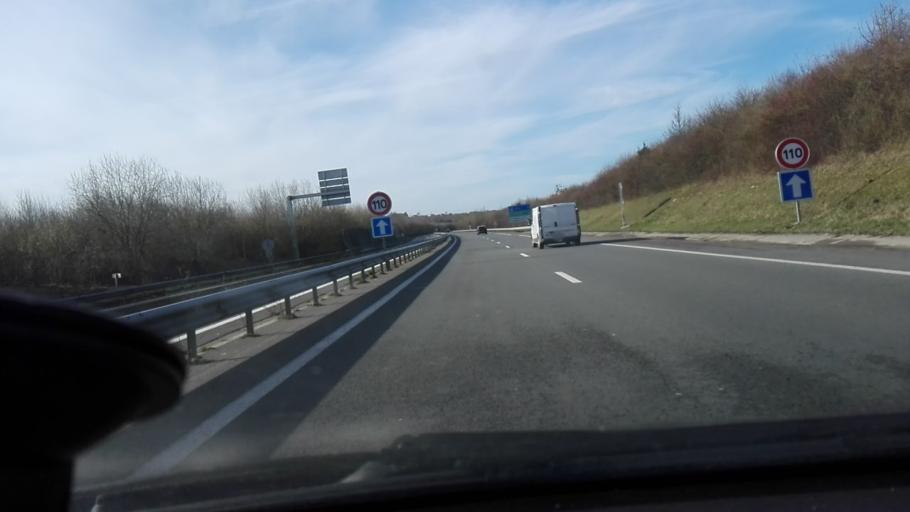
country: FR
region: Nord-Pas-de-Calais
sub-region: Departement du Pas-de-Calais
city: Hardinghen
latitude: 50.7410
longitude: 1.8022
